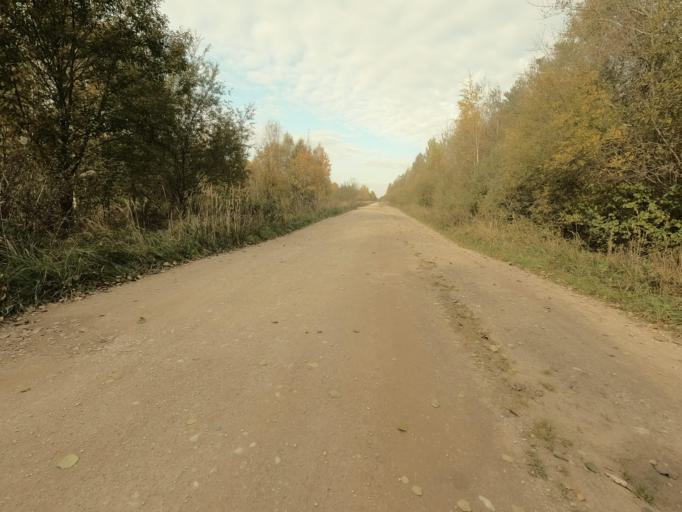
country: RU
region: Novgorod
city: Volkhovskiy
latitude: 58.9104
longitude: 31.0395
